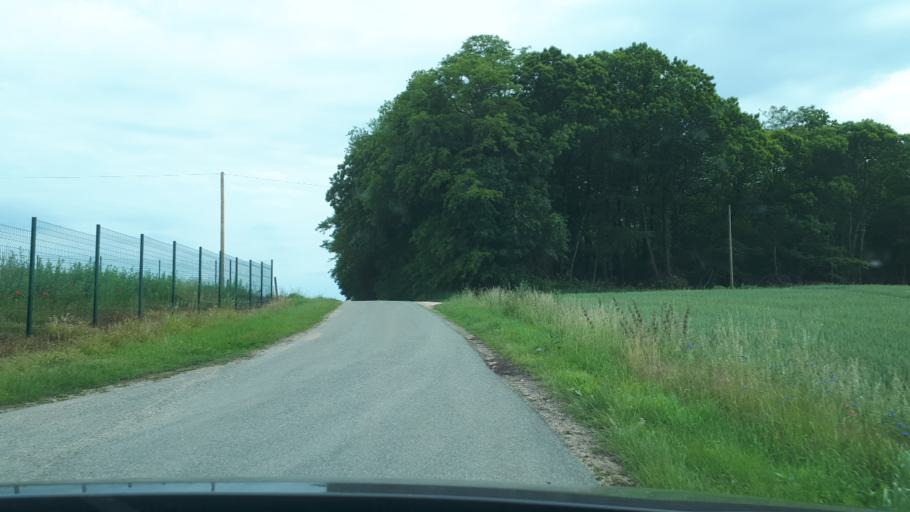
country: FR
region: Centre
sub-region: Departement du Cher
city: Sancerre
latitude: 47.3123
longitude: 2.7423
